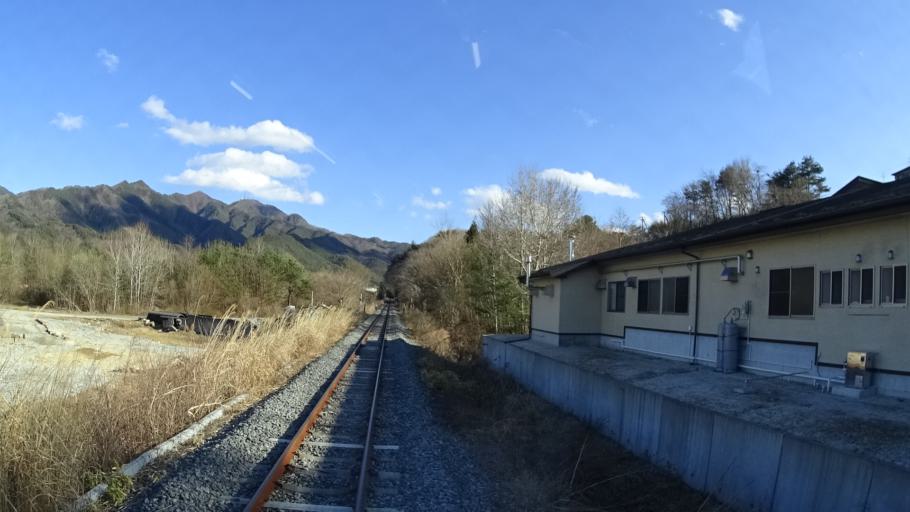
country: JP
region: Iwate
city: Miyako
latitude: 39.5630
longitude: 141.9343
